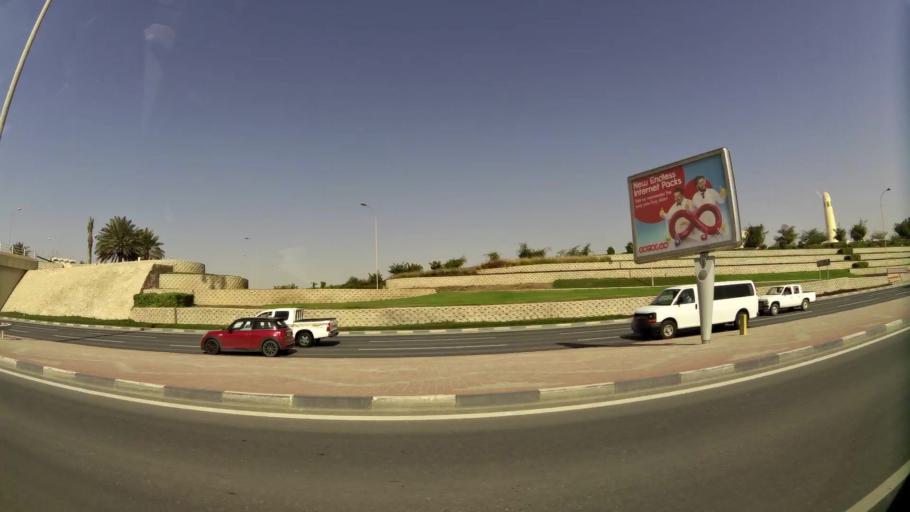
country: QA
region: Baladiyat ad Dawhah
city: Doha
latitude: 25.3145
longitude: 51.5061
